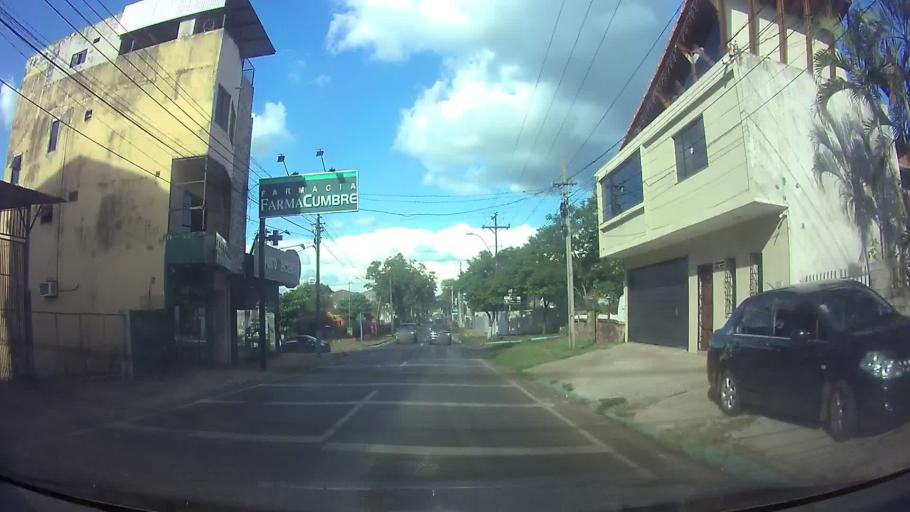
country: PY
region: Cordillera
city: Caacupe
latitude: -25.3876
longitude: -57.1460
